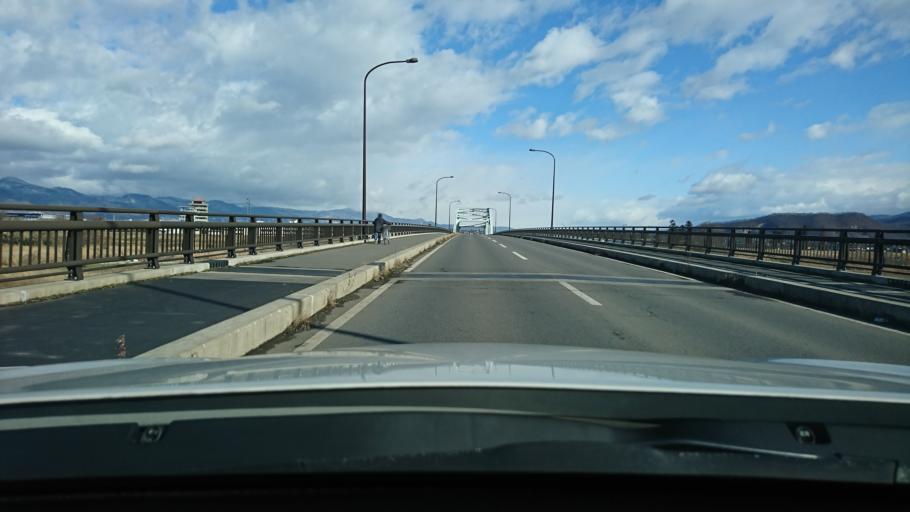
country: JP
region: Nagano
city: Nagano-shi
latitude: 36.5669
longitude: 138.1739
